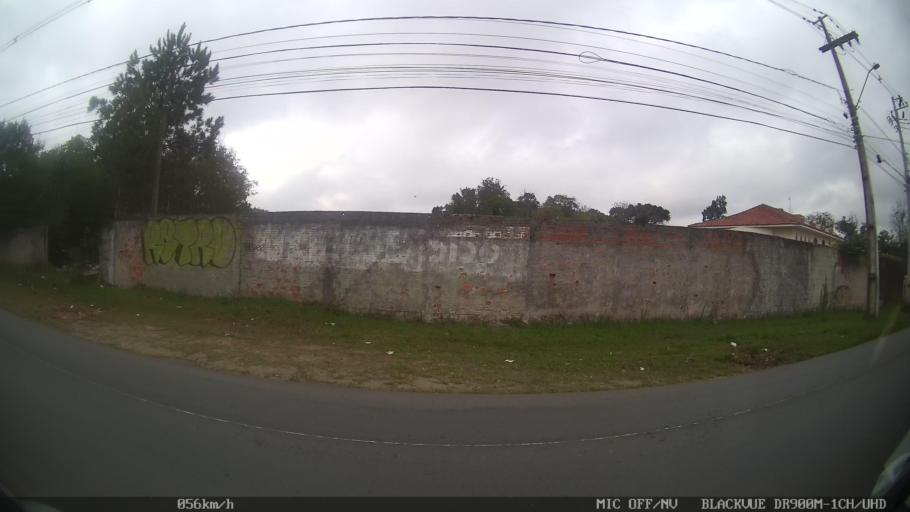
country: BR
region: Parana
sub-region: Almirante Tamandare
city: Almirante Tamandare
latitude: -25.3641
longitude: -49.2718
